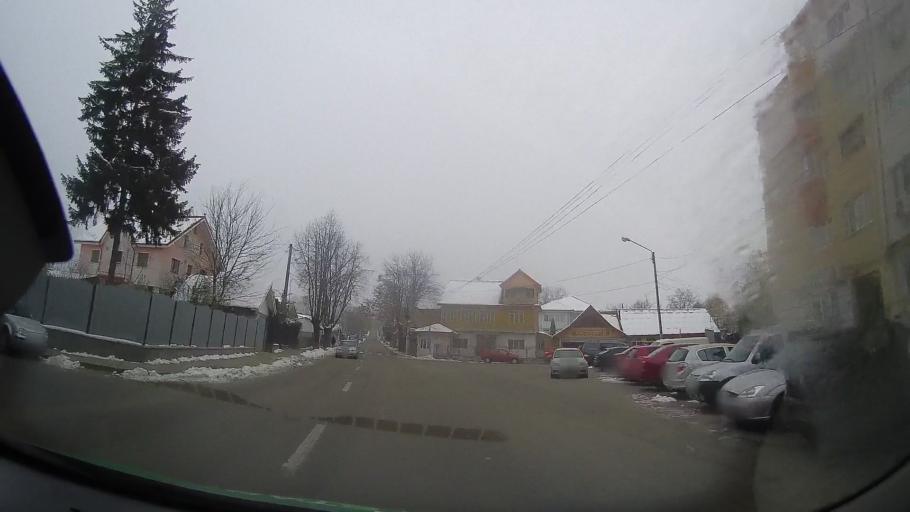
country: RO
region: Vaslui
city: Vaslui
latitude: 46.6501
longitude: 27.7318
